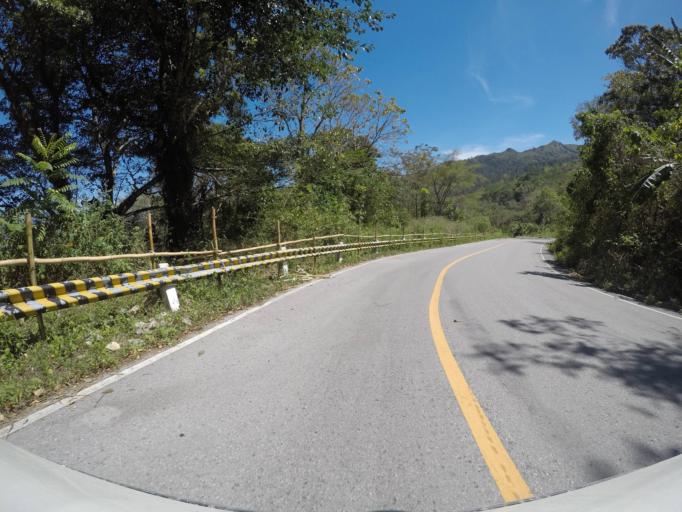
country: TL
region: Manatuto
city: Manatuto
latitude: -8.8219
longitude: 125.9790
